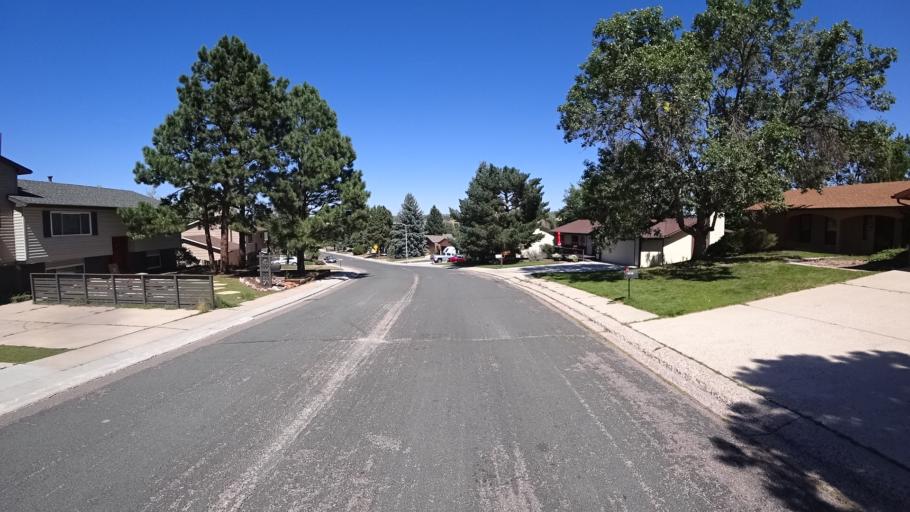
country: US
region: Colorado
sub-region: El Paso County
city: Colorado Springs
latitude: 38.9225
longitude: -104.7976
